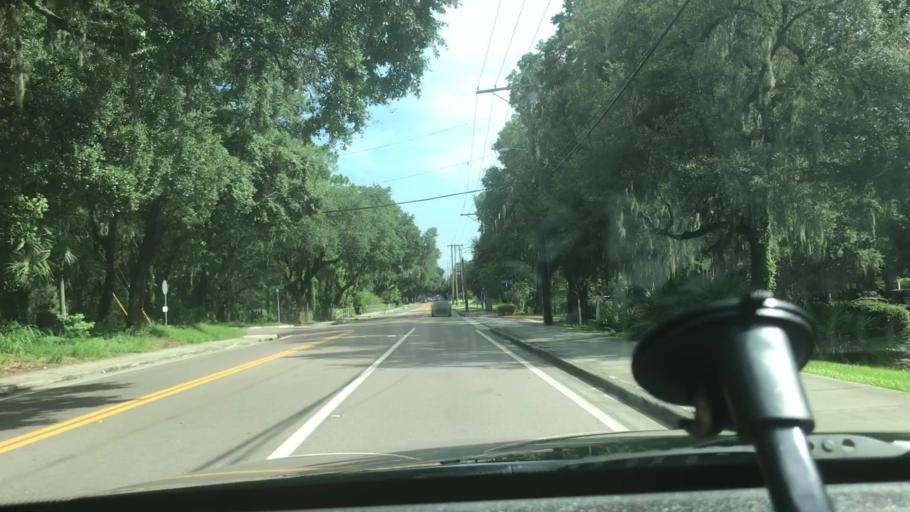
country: US
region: Florida
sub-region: Hillsborough County
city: Mango
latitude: 27.9892
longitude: -82.3188
